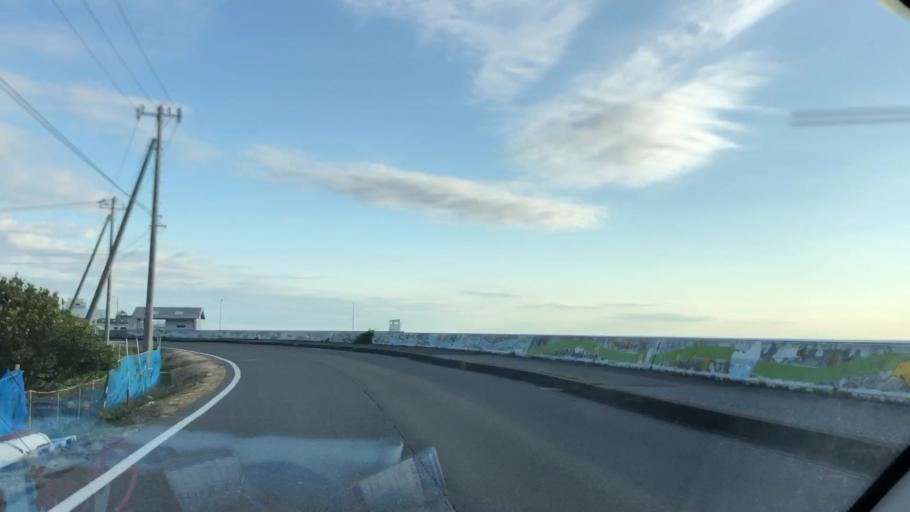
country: JP
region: Chiba
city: Tateyama
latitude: 34.9347
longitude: 139.9556
